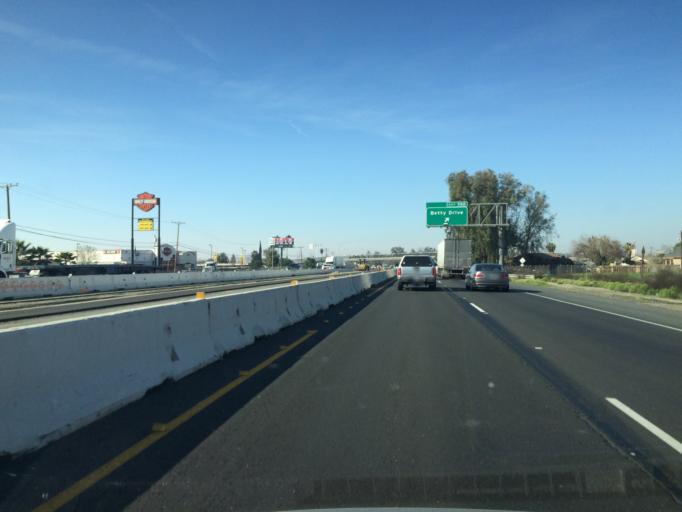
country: US
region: California
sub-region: Tulare County
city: Goshen
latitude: 36.3457
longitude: -119.4231
